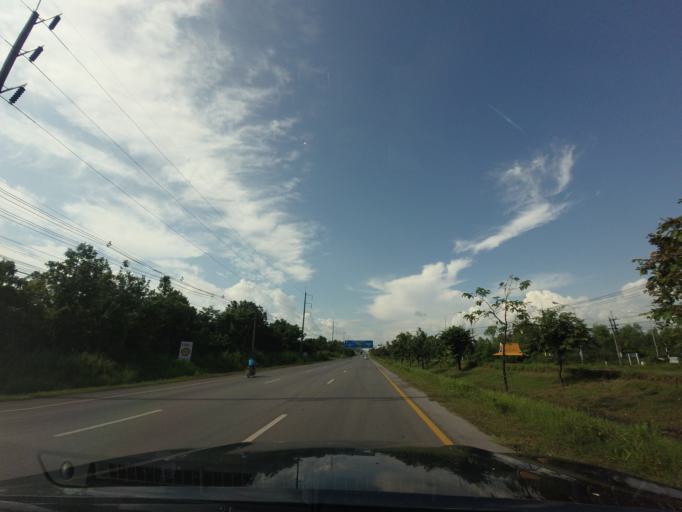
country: TH
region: Nong Khai
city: Nong Khai
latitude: 17.7965
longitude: 102.7623
